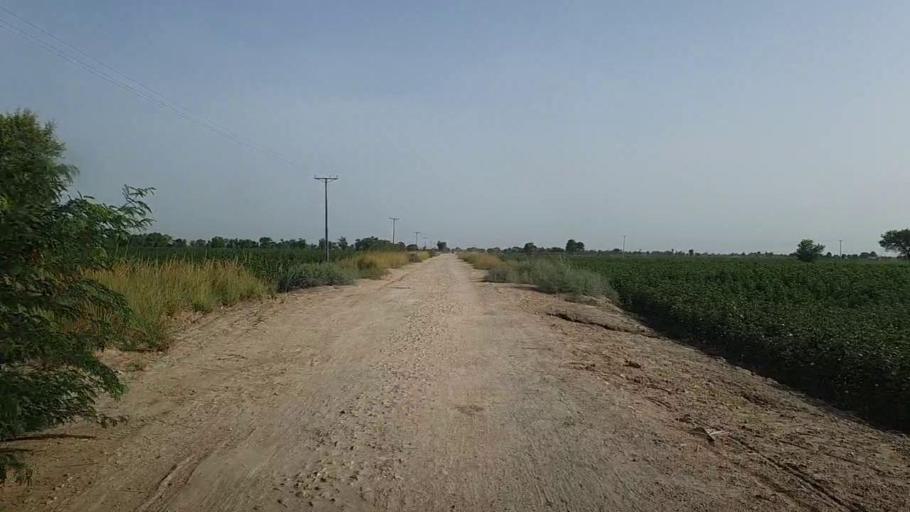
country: PK
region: Sindh
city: Pad Idan
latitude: 26.7674
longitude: 68.2572
